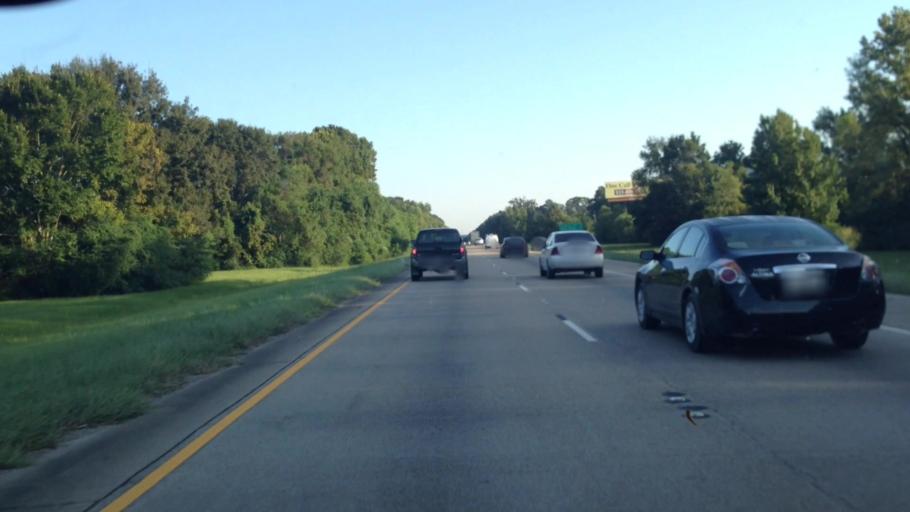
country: US
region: Louisiana
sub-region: Ascension Parish
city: Prairieville
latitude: 30.2818
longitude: -90.9889
